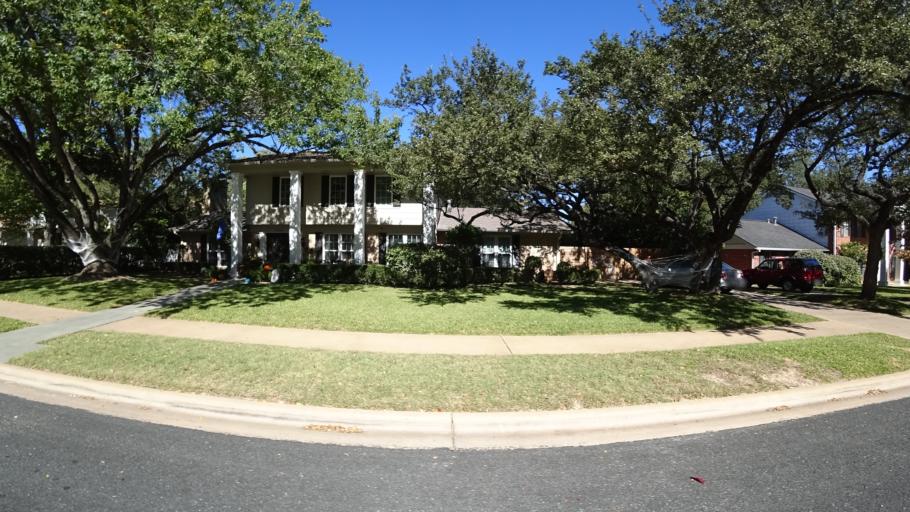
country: US
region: Texas
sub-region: Travis County
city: West Lake Hills
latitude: 30.3595
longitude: -97.7554
